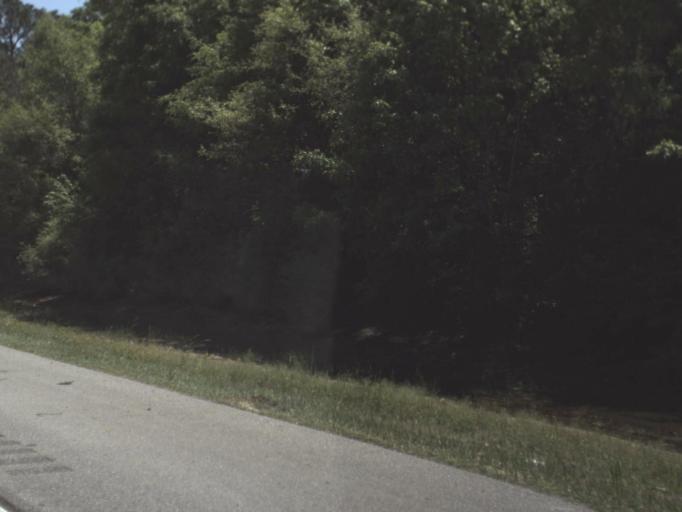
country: US
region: Florida
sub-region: Escambia County
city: Ensley
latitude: 30.5037
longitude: -87.2515
